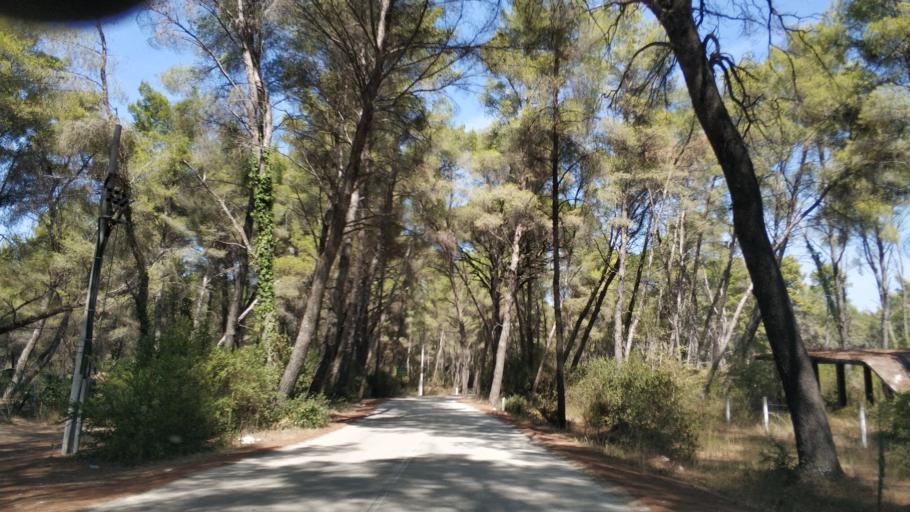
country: AL
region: Fier
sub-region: Rrethi i Lushnjes
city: Divjake
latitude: 40.9756
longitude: 19.4810
